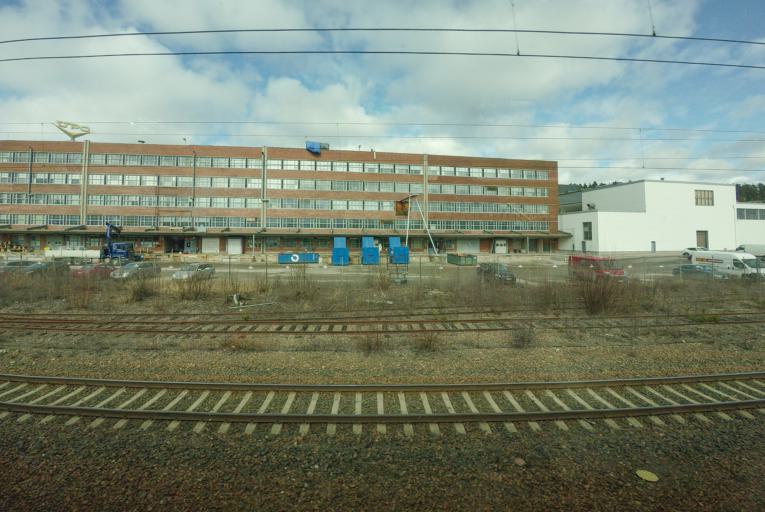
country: FI
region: Paijanne Tavastia
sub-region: Lahti
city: Lahti
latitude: 60.9754
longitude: 25.6770
